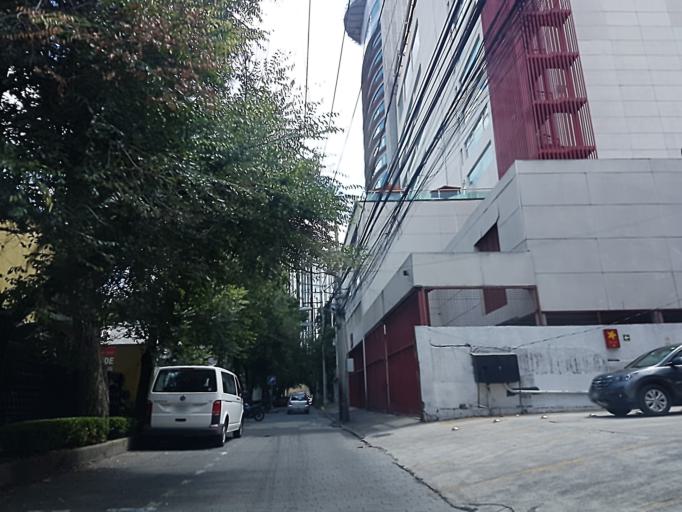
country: MX
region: Mexico City
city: Alvaro Obregon
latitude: 19.3545
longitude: -99.1846
